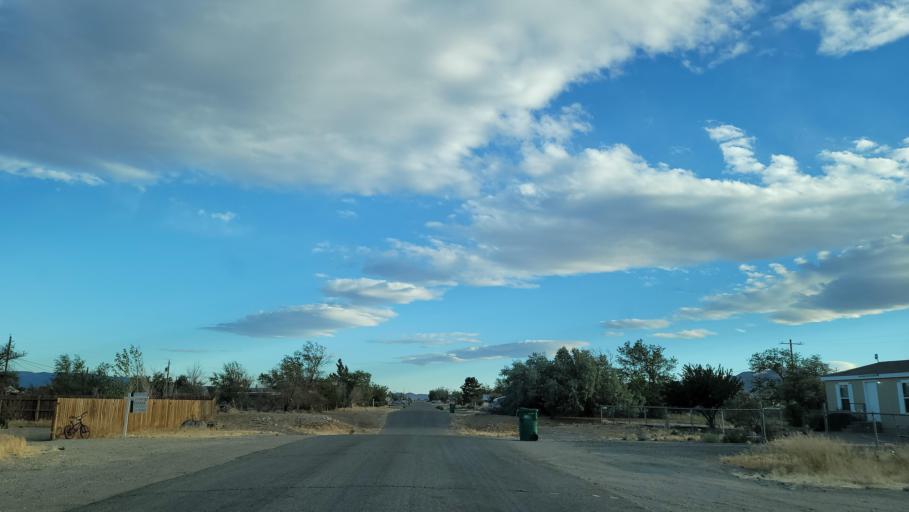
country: US
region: Nevada
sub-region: Lyon County
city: Silver Springs
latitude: 39.4113
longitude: -119.2216
